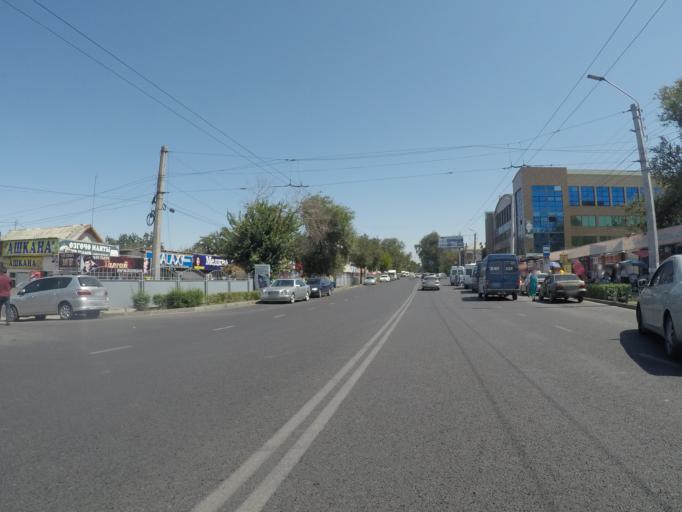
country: KG
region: Chuy
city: Bishkek
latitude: 42.8774
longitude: 74.5700
